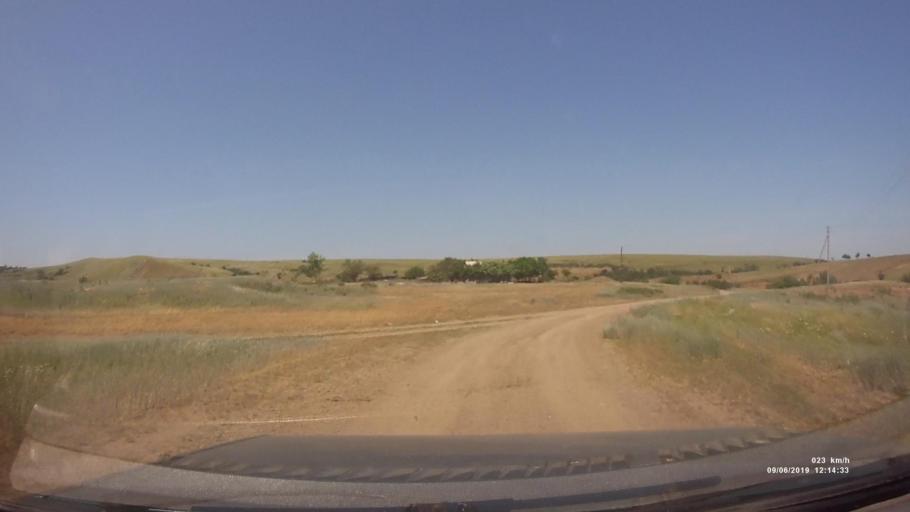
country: RU
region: Rostov
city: Staraya Stanitsa
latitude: 48.2523
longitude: 40.3228
